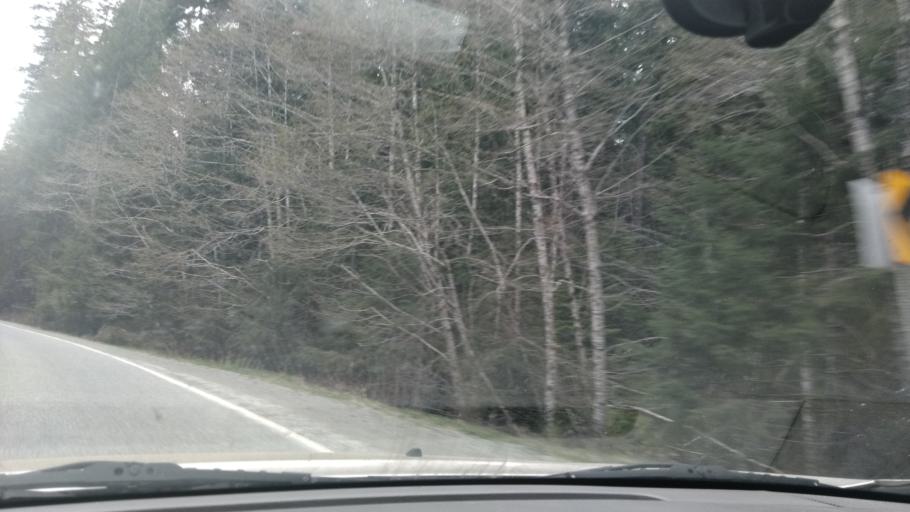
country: CA
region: British Columbia
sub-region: Regional District of Alberni-Clayoquot
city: Tofino
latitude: 49.8414
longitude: -125.9160
